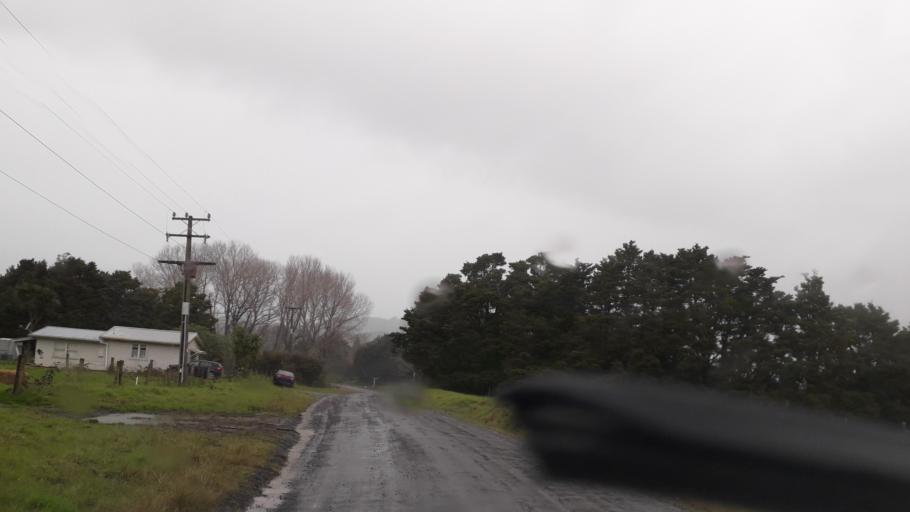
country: NZ
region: Northland
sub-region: Far North District
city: Waimate North
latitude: -35.5037
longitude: 173.7006
